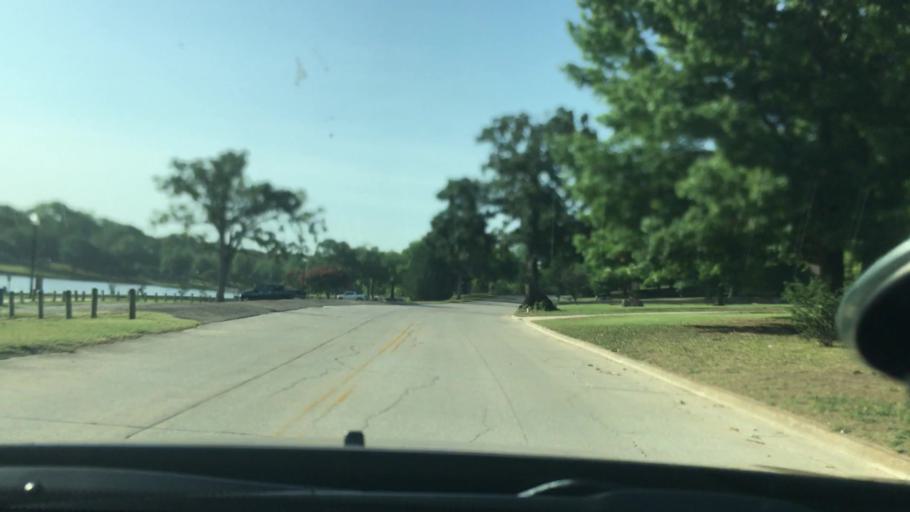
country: US
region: Oklahoma
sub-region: Pontotoc County
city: Ada
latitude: 34.7642
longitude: -96.6561
